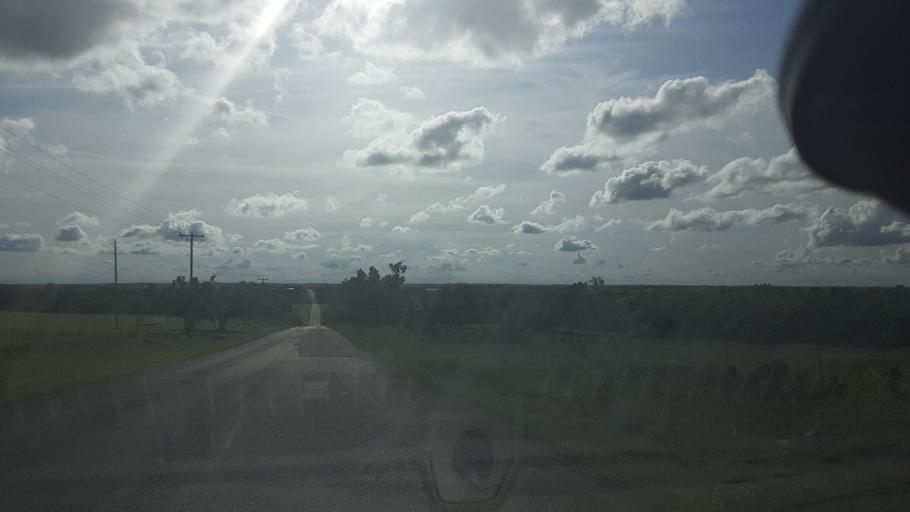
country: US
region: Oklahoma
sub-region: Logan County
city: Langston
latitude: 36.0577
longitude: -97.3638
